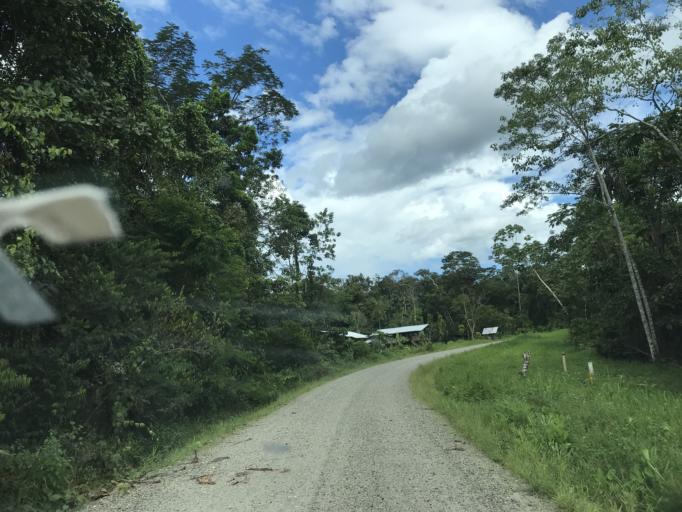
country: EC
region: Orellana
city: Puerto Francisco de Orellana
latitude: -0.6122
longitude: -76.4655
